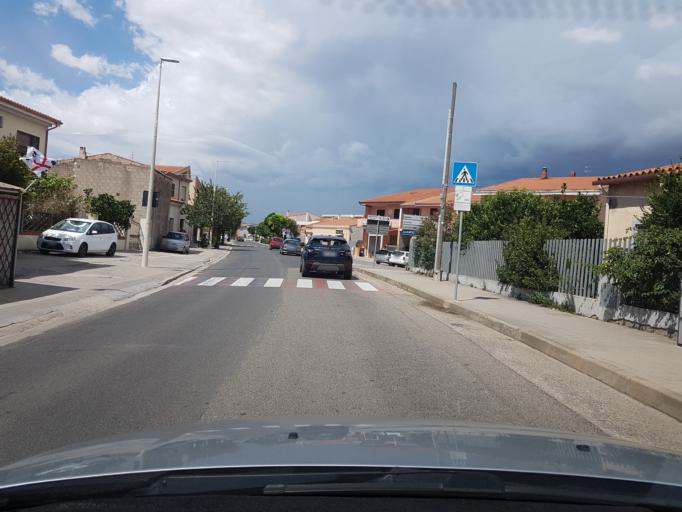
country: IT
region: Sardinia
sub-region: Provincia di Oristano
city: Riola Sardo
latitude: 39.9905
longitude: 8.5419
